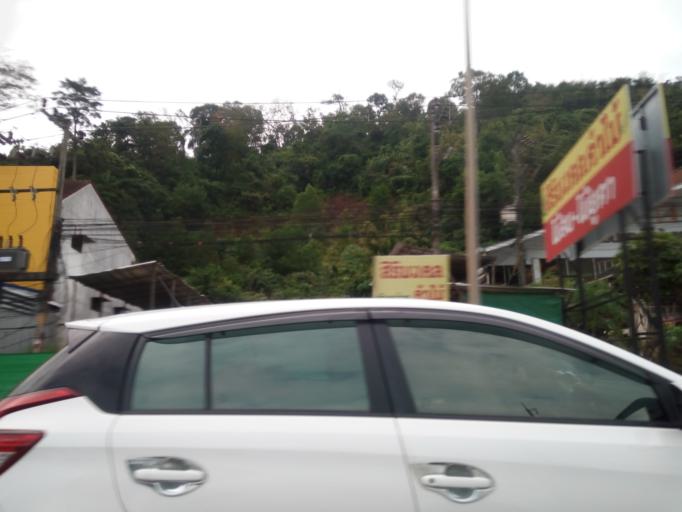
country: TH
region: Phuket
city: Wichit
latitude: 7.9124
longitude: 98.3677
